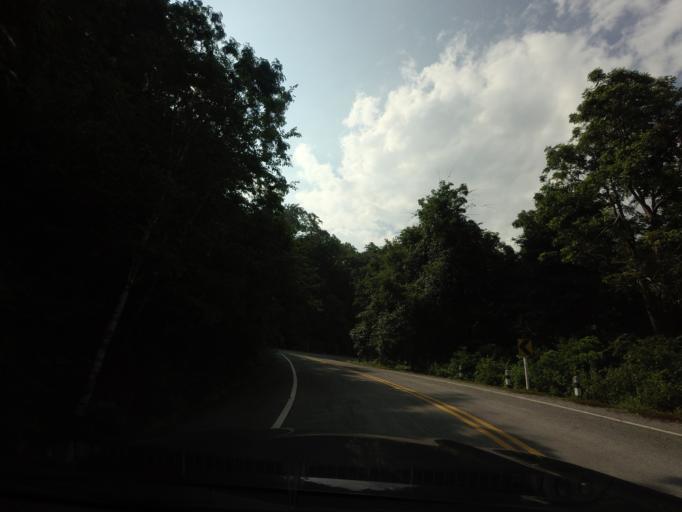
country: TH
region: Nan
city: Na Noi
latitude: 18.2747
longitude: 100.9682
